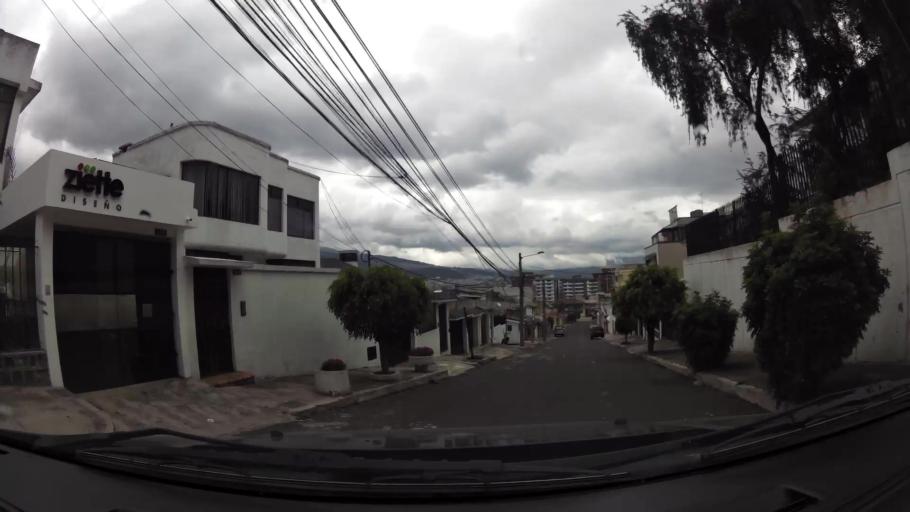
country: EC
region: Pichincha
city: Quito
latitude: -0.1746
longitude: -78.4724
